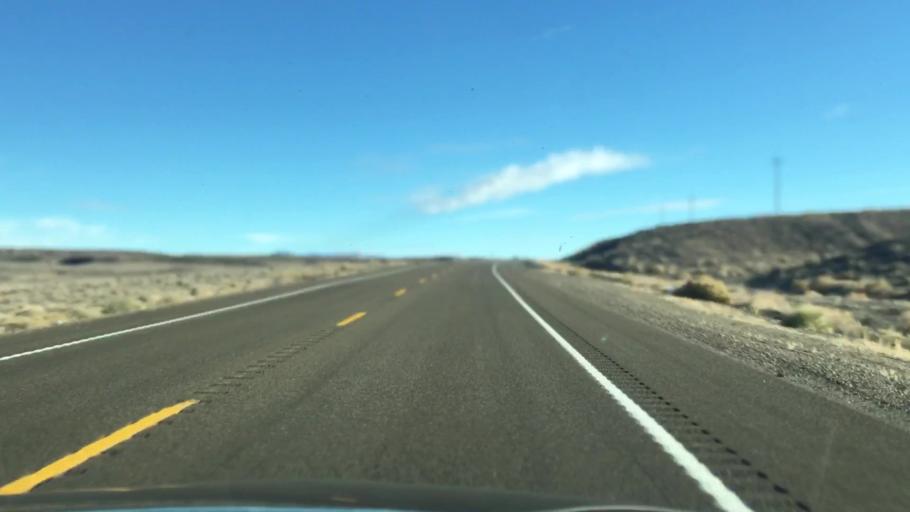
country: US
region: Nevada
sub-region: Mineral County
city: Hawthorne
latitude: 38.2312
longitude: -118.0204
